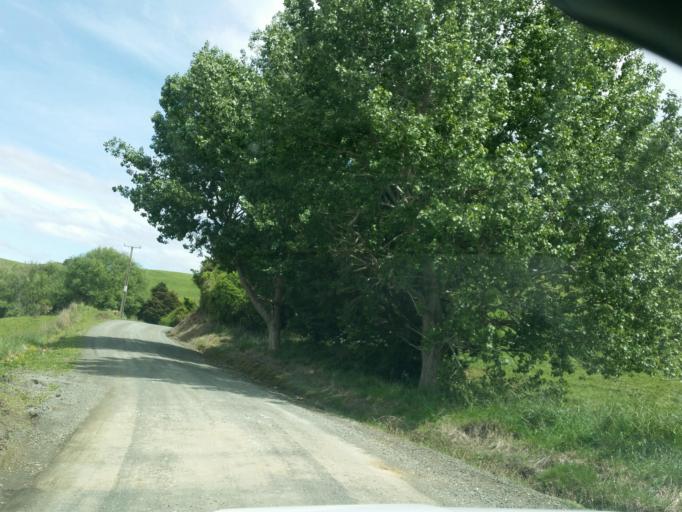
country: NZ
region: Northland
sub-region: Whangarei
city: Maungatapere
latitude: -35.9014
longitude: 174.1443
